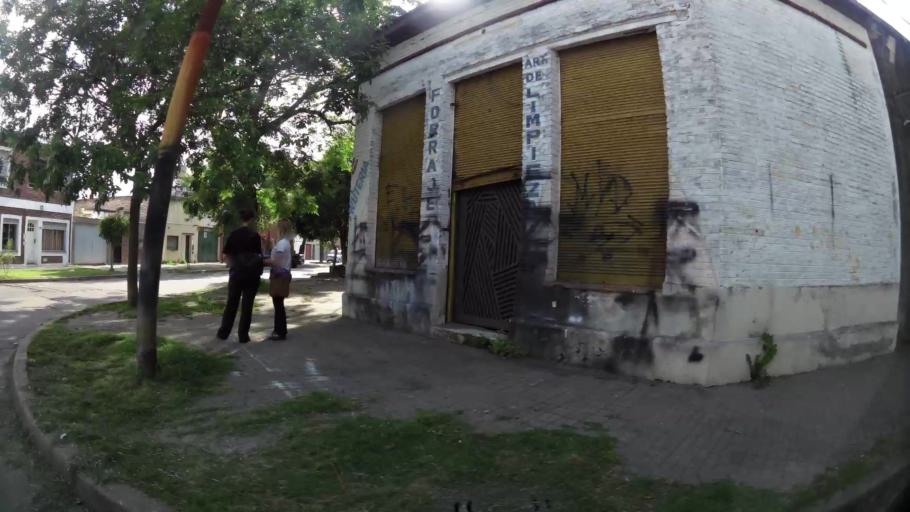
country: AR
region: Santa Fe
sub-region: Departamento de Rosario
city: Rosario
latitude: -32.9211
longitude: -60.6891
